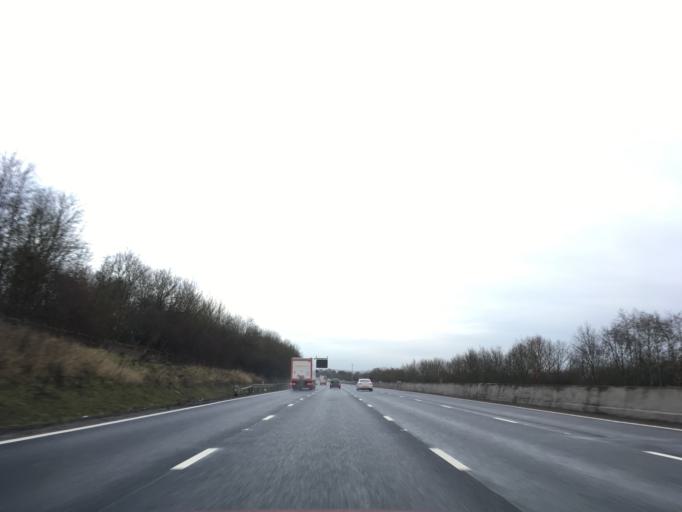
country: GB
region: England
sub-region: Worcestershire
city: Droitwich
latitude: 52.2347
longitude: -2.1381
